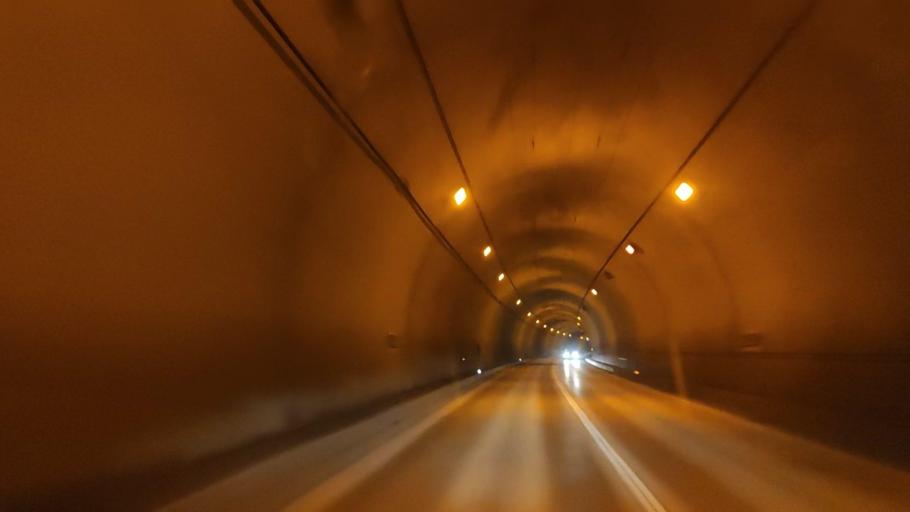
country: JP
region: Tottori
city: Kurayoshi
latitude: 35.3164
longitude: 133.7553
